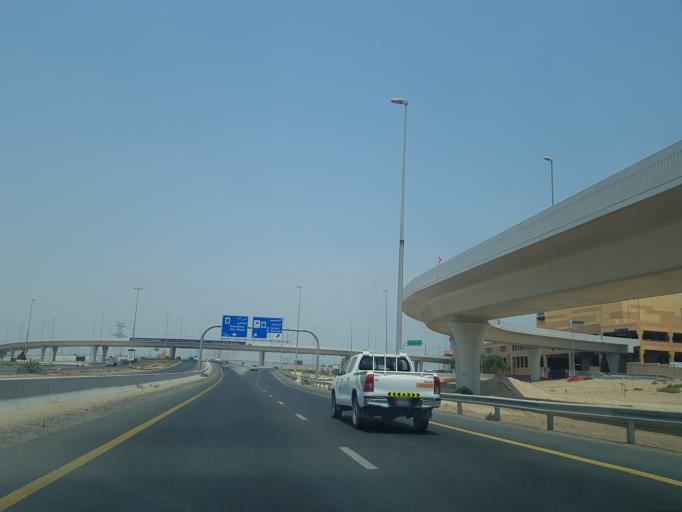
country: AE
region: Ash Shariqah
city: Sharjah
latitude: 25.2122
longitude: 55.4088
